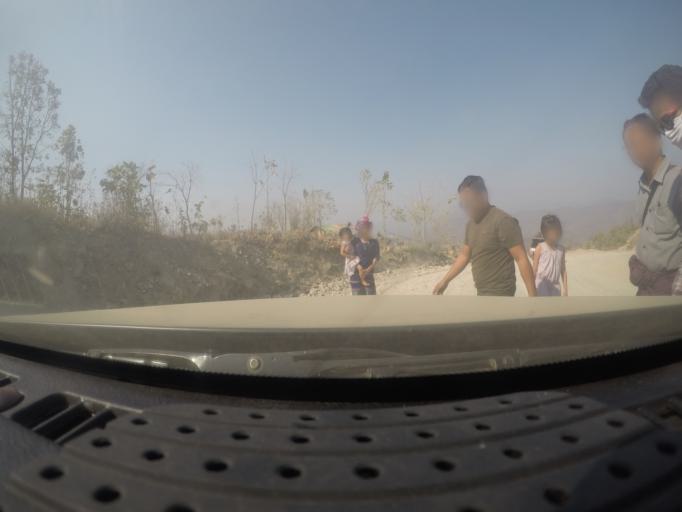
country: MM
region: Mandalay
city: Kyaukse
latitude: 21.3829
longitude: 96.3823
